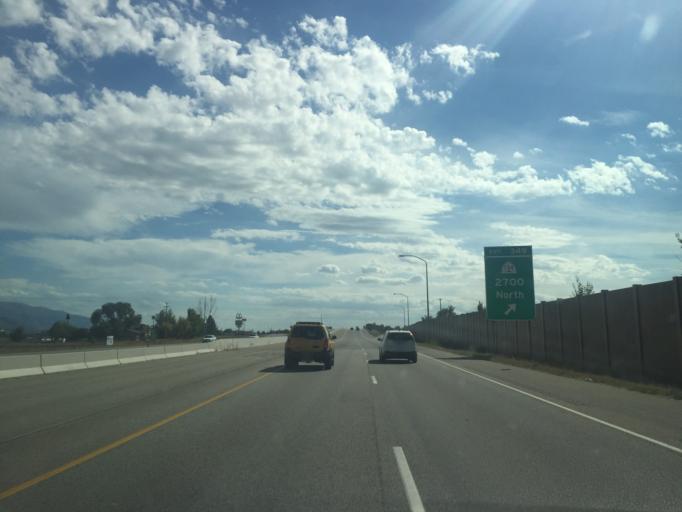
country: US
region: Utah
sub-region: Weber County
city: Farr West
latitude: 41.3125
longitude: -112.0261
